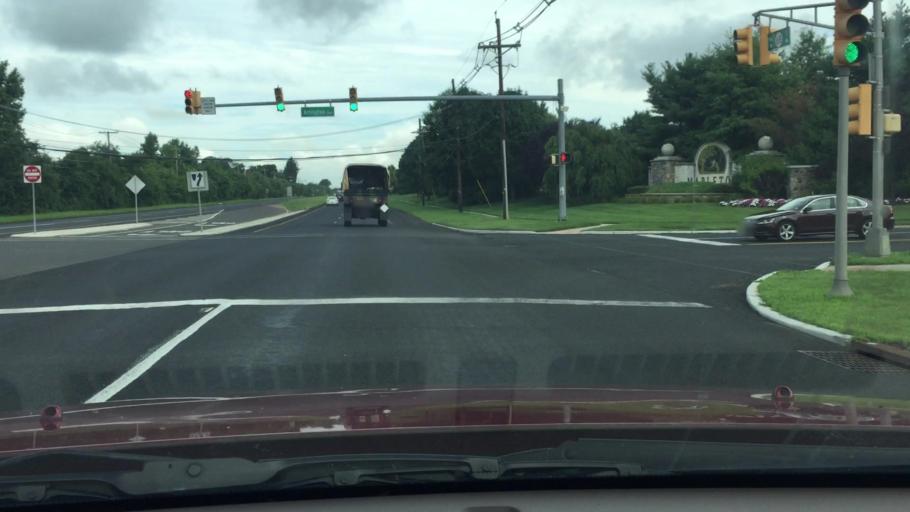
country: US
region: New Jersey
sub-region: Burlington County
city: Bordentown
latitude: 40.0842
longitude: -74.6706
